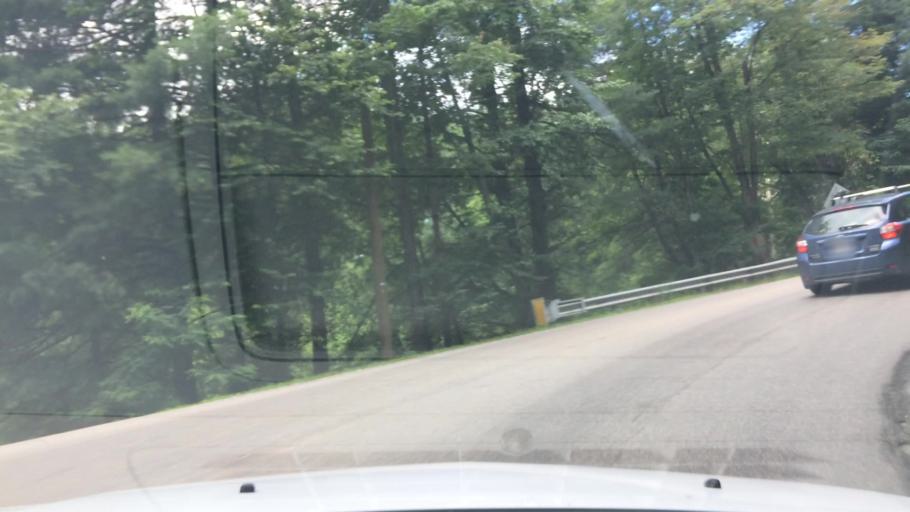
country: US
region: North Carolina
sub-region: Watauga County
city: Boone
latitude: 36.2067
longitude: -81.6312
